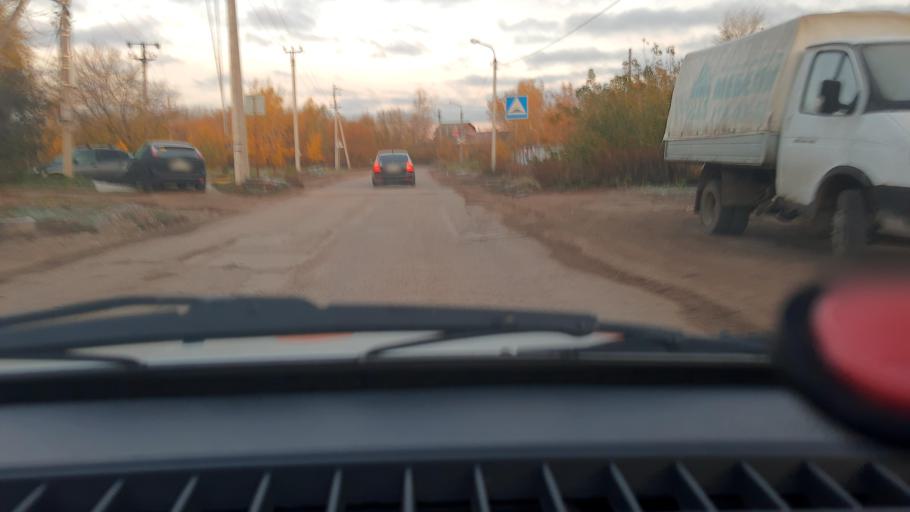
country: RU
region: Bashkortostan
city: Mikhaylovka
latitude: 54.7500
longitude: 55.9077
